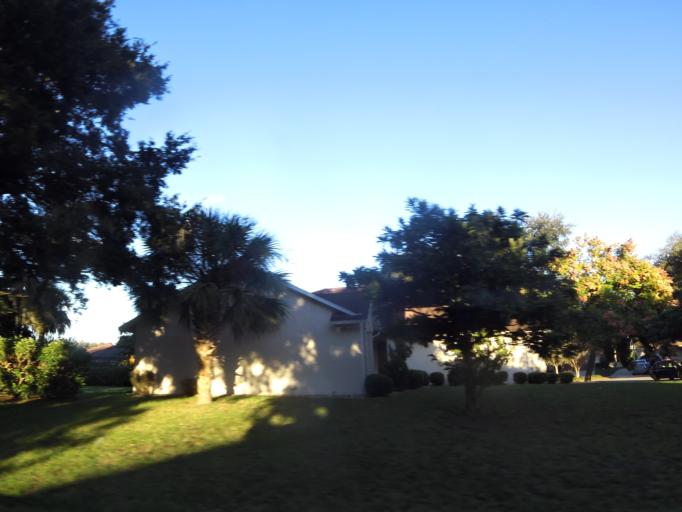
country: US
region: Florida
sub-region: Flagler County
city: Palm Coast
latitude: 29.5616
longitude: -81.2054
